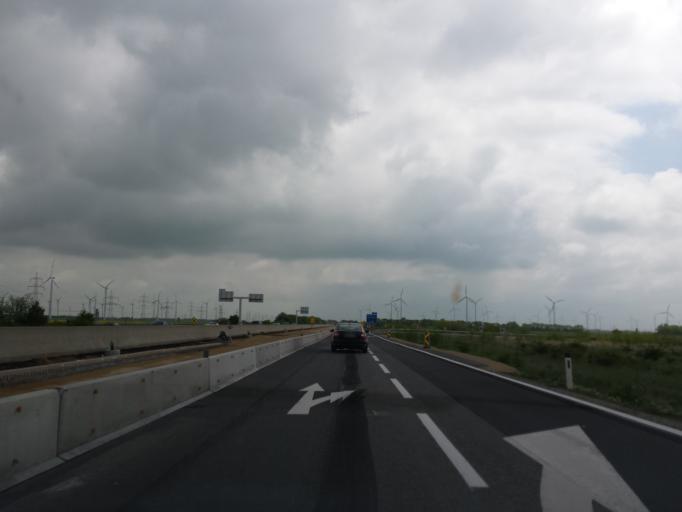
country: AT
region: Burgenland
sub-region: Politischer Bezirk Neusiedl am See
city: Parndorf
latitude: 47.9741
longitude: 16.8538
